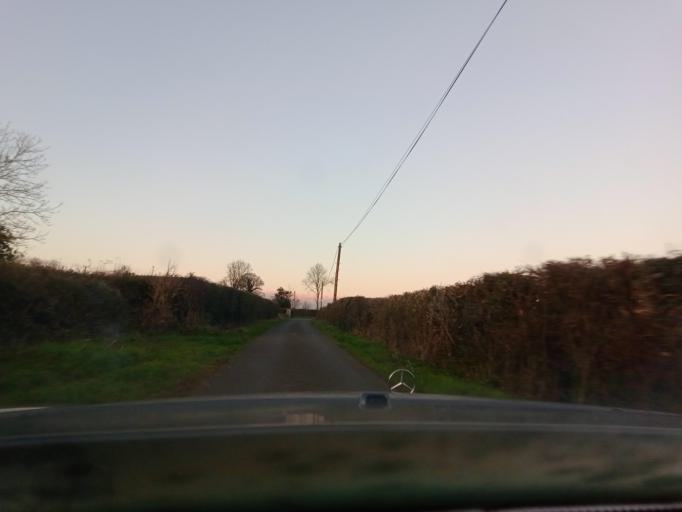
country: IE
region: Leinster
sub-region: Kilkenny
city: Graiguenamanagh
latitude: 52.5699
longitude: -6.9578
